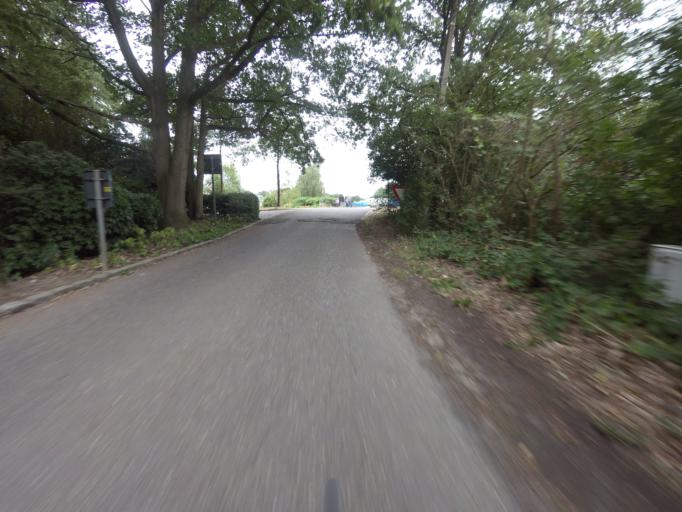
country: BE
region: Flanders
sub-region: Provincie Antwerpen
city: Schoten
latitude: 51.2775
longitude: 4.5283
